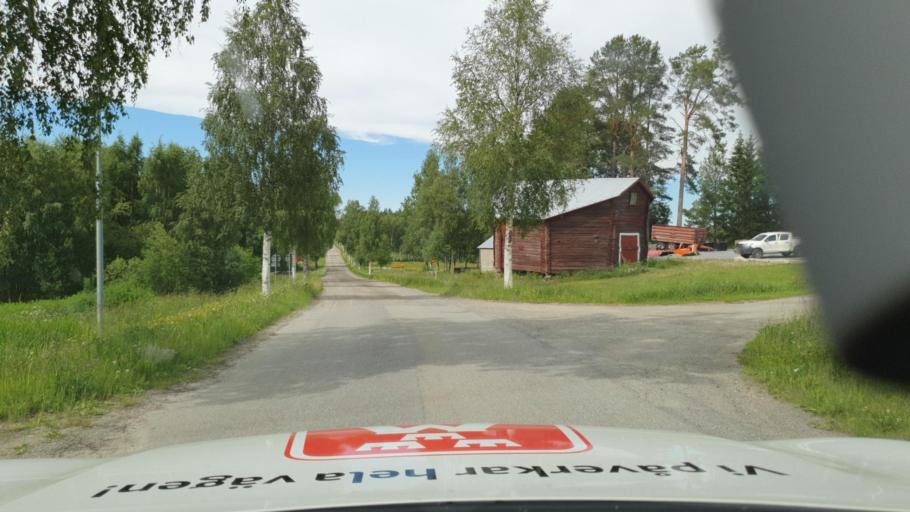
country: SE
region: Vaesterbotten
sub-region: Skelleftea Kommun
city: Burtraesk
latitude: 64.4551
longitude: 20.4791
